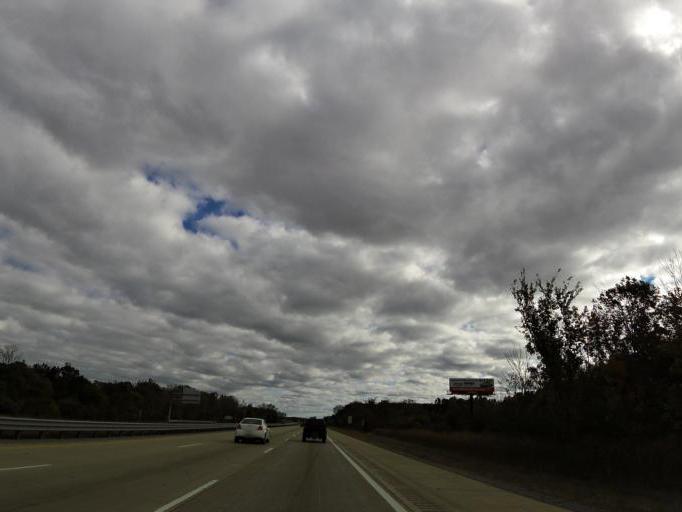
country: US
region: Michigan
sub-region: Genesee County
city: Flint
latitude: 42.9777
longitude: -83.7551
